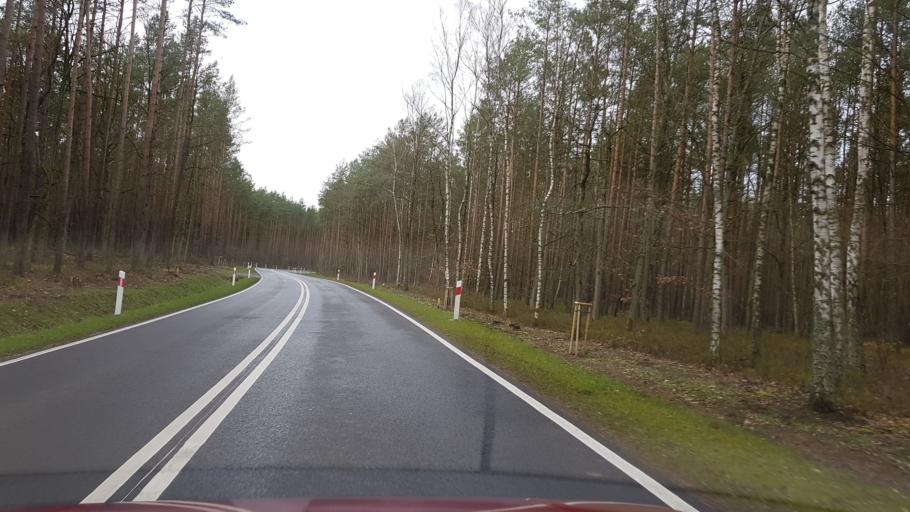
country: PL
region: West Pomeranian Voivodeship
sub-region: Powiat policki
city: Police
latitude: 53.6591
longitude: 14.4684
